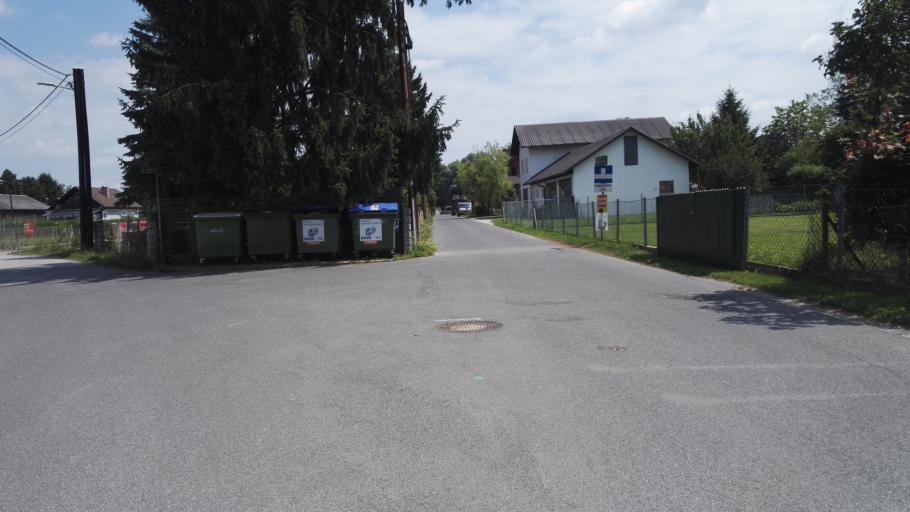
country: AT
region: Styria
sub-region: Politischer Bezirk Graz-Umgebung
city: Feldkirchen bei Graz
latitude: 47.0210
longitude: 15.4517
